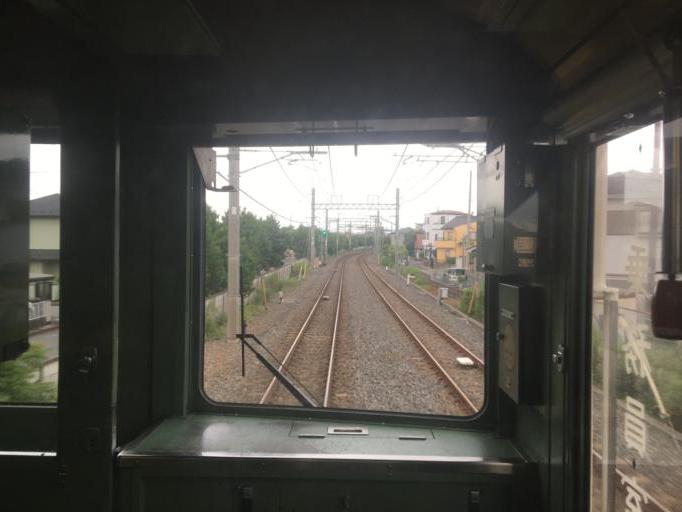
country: JP
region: Saitama
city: Iwatsuki
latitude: 35.9592
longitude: 139.7071
